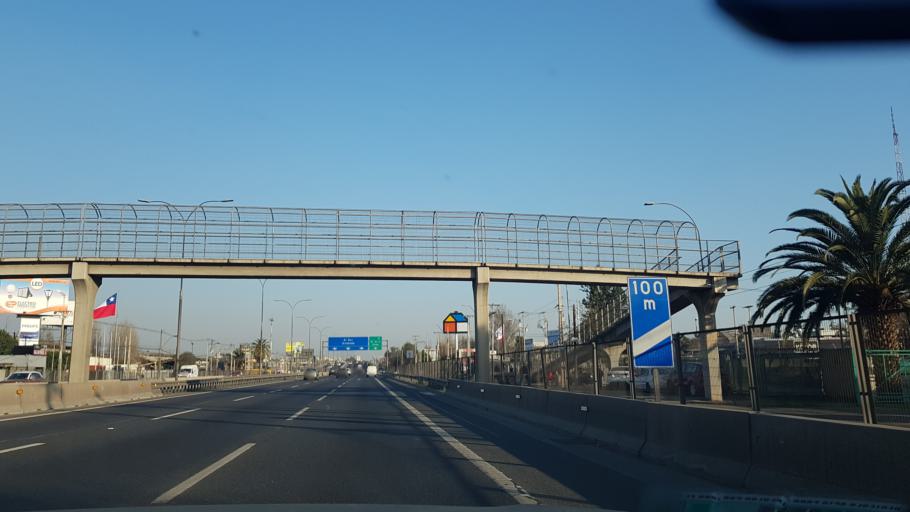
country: CL
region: Santiago Metropolitan
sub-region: Provincia de Santiago
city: Lo Prado
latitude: -33.3978
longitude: -70.6852
